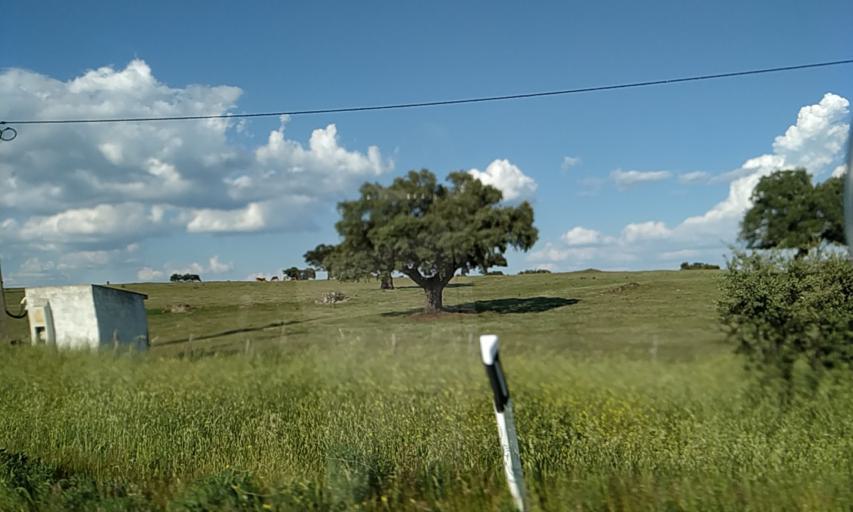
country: PT
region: Portalegre
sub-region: Portalegre
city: Urra
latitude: 39.1310
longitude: -7.4480
